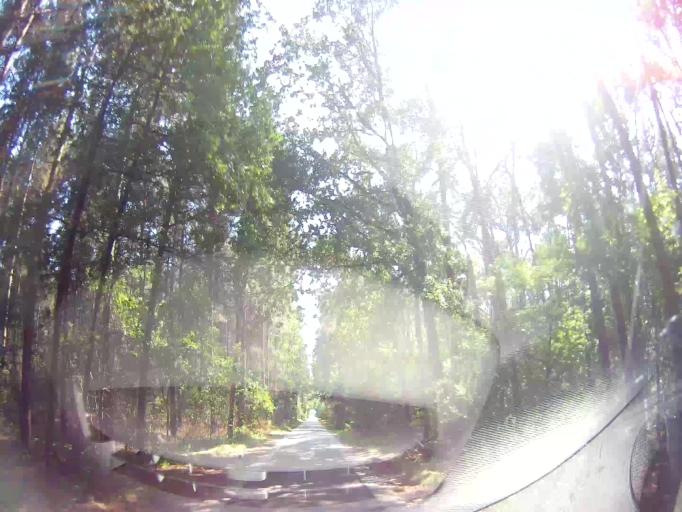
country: BE
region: Flanders
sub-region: Provincie Antwerpen
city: Retie
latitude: 51.2662
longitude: 5.0441
